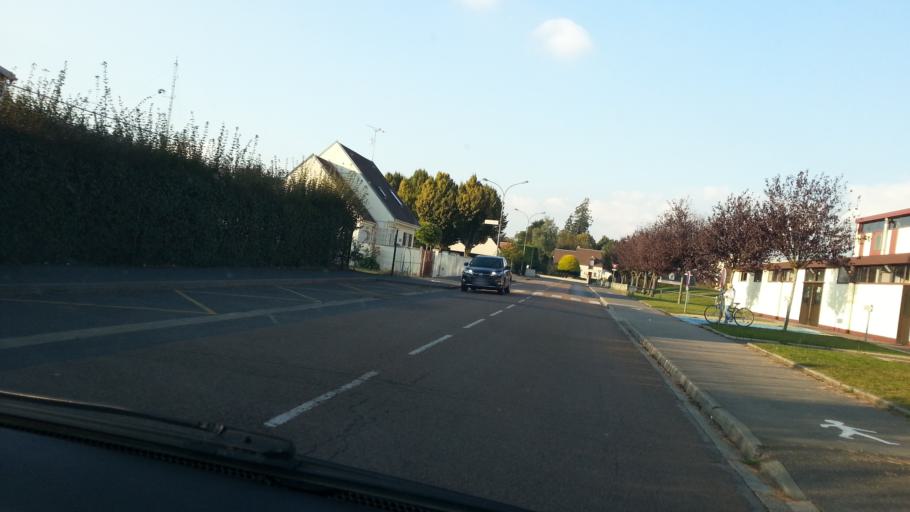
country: FR
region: Picardie
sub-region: Departement de l'Oise
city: Estrees-Saint-Denis
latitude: 49.4294
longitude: 2.6427
